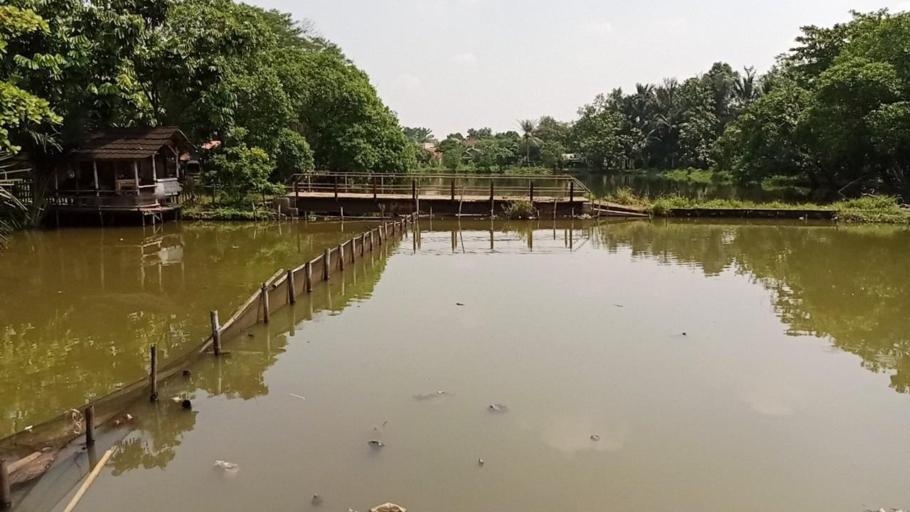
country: ID
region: West Java
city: Parung
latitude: -6.4248
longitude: 106.7504
